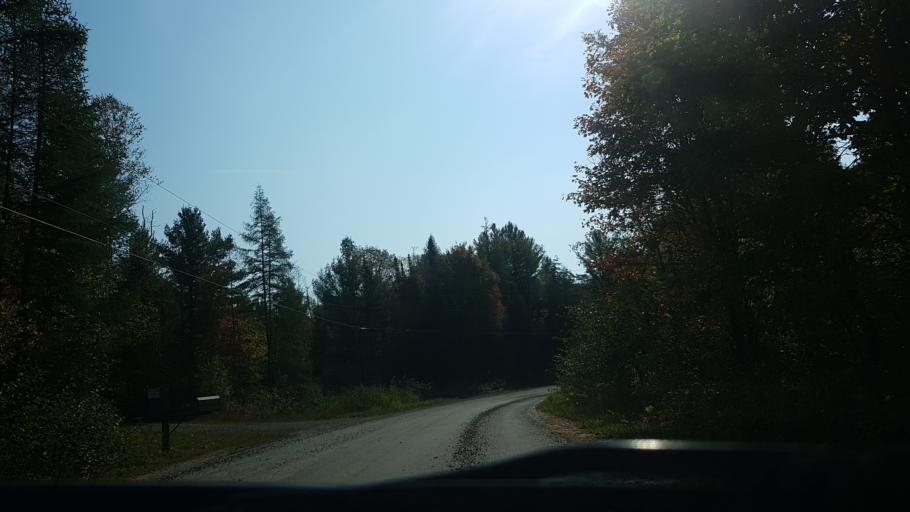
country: CA
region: Ontario
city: Bracebridge
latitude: 44.9396
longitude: -79.2395
